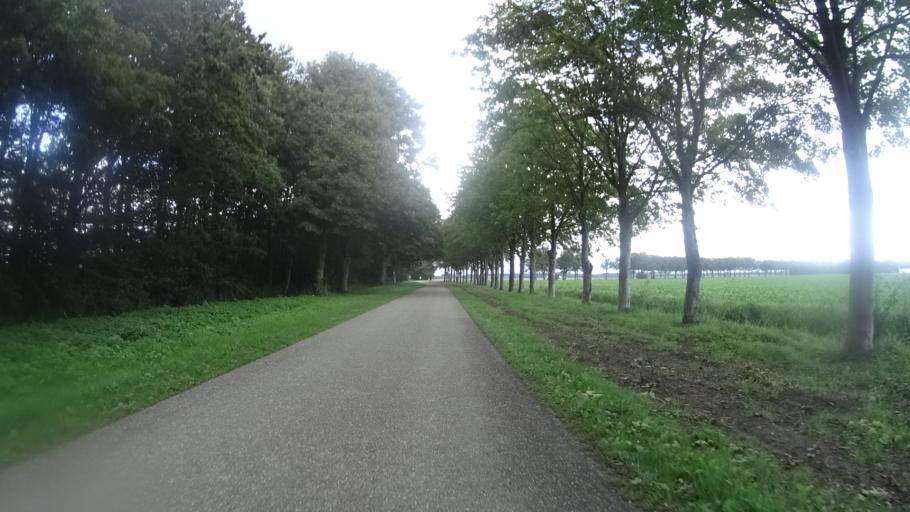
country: NL
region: North Holland
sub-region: Gemeente Hollands Kroon
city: Den Oever
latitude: 52.8914
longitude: 4.9756
